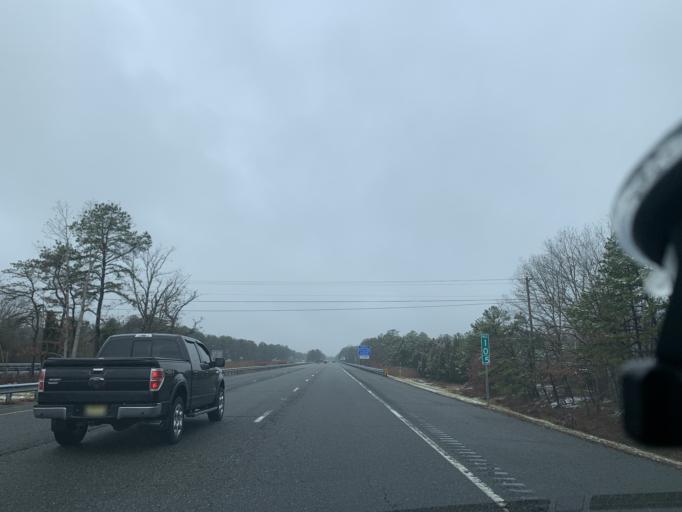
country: US
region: New Jersey
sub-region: Atlantic County
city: Pomona
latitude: 39.4405
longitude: -74.6026
